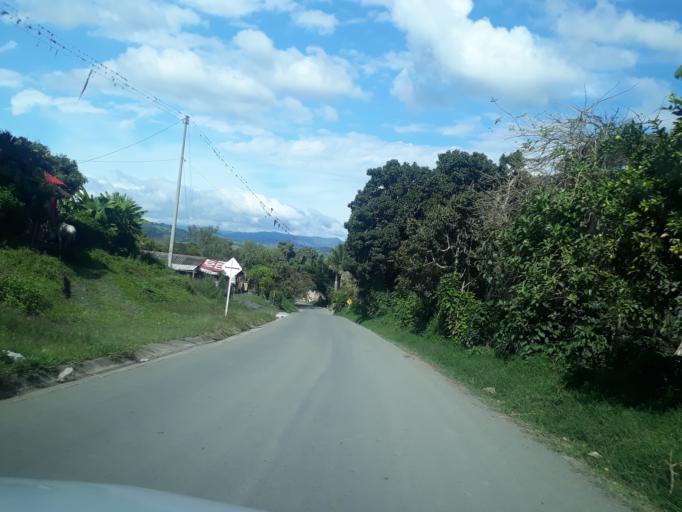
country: CO
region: Santander
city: Velez
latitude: 6.0428
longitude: -73.6522
